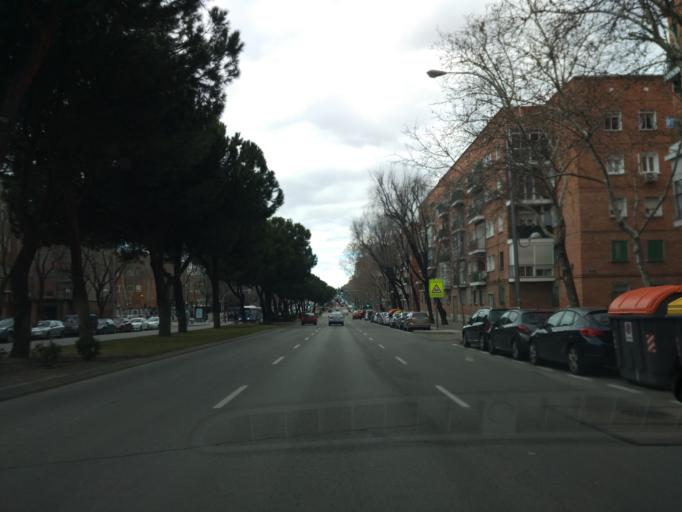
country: ES
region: Madrid
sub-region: Provincia de Madrid
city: San Blas
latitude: 40.4284
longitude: -3.6310
